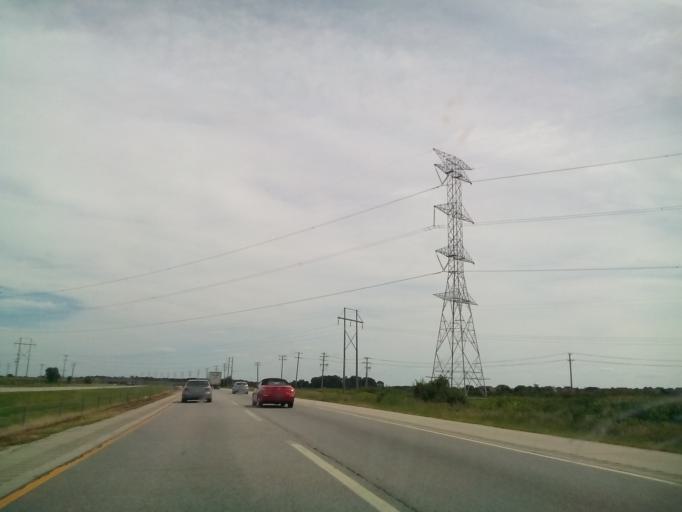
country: US
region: Illinois
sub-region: Kane County
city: Sugar Grove
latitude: 41.8065
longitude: -88.4378
